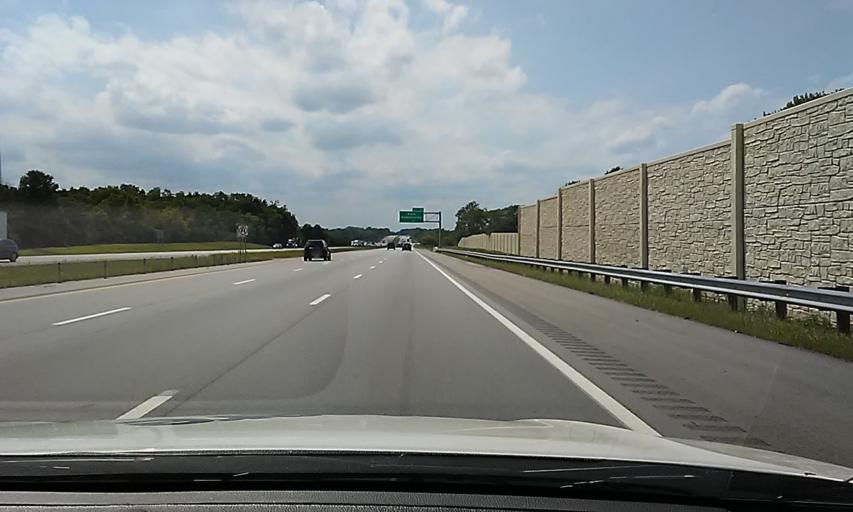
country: US
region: Ohio
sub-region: Clark County
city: Enon
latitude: 39.8926
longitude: -83.9214
